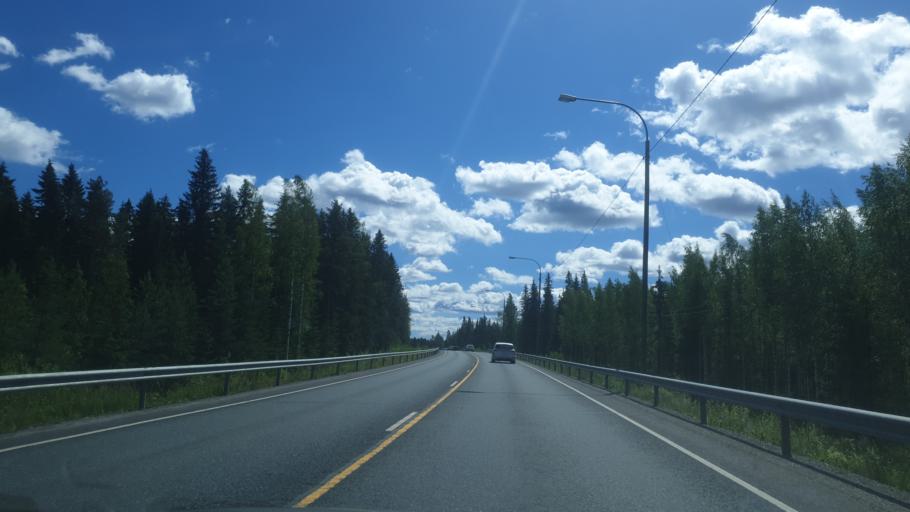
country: FI
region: Northern Savo
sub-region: Varkaus
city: Leppaevirta
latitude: 62.5451
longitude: 27.6255
